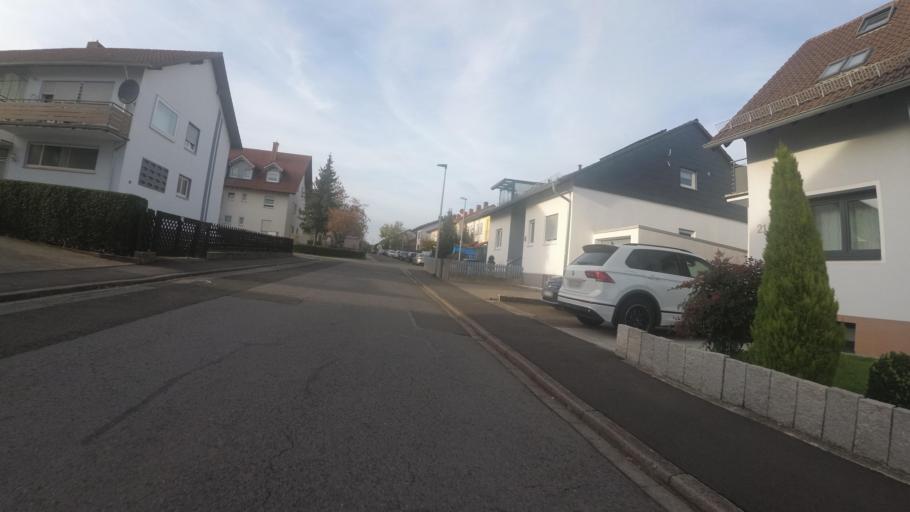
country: DE
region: Rheinland-Pfalz
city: Ramstein-Miesenbach
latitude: 49.4419
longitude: 7.5485
